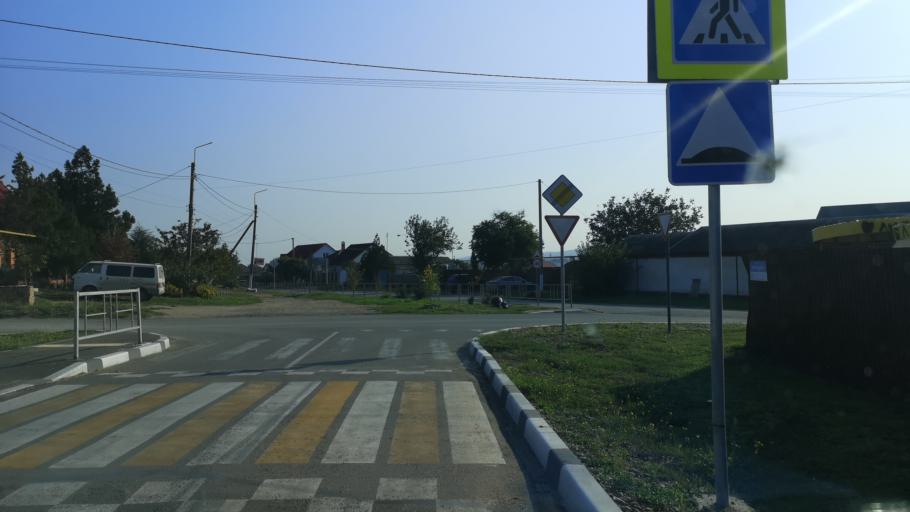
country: RU
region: Krasnodarskiy
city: Taman'
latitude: 45.2141
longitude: 36.7023
